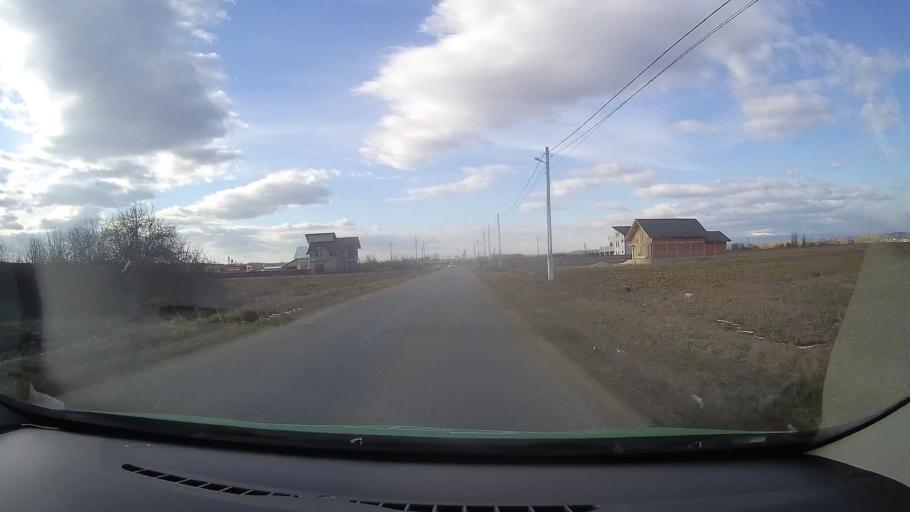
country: RO
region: Dambovita
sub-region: Comuna Ulmi
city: Ulmi
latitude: 44.8969
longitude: 25.5000
